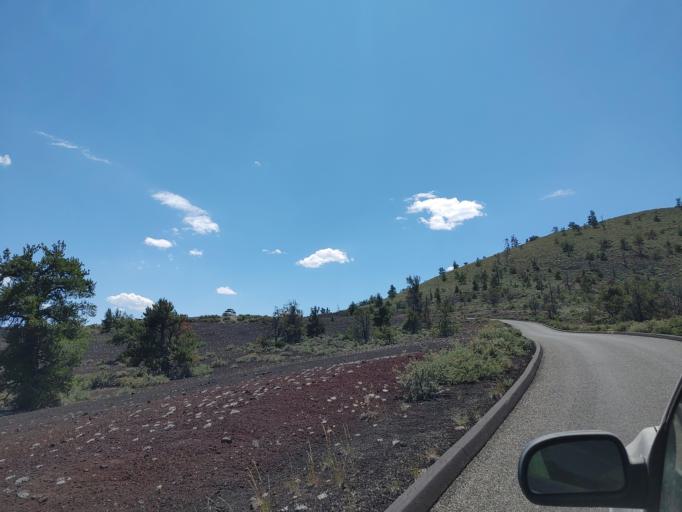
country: US
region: Idaho
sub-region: Butte County
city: Arco
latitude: 43.4463
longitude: -113.5553
